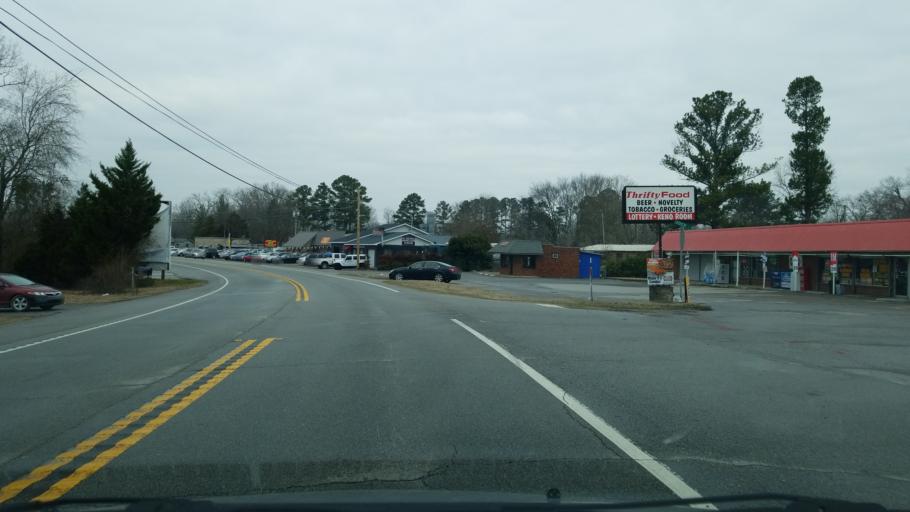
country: US
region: Georgia
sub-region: Catoosa County
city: Indian Springs
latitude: 34.9589
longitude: -85.1651
